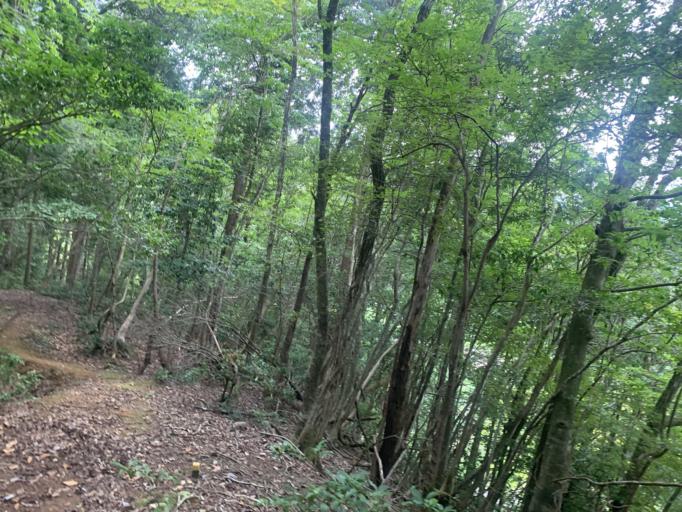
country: JP
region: Kyoto
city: Miyazu
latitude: 35.4473
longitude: 135.1631
